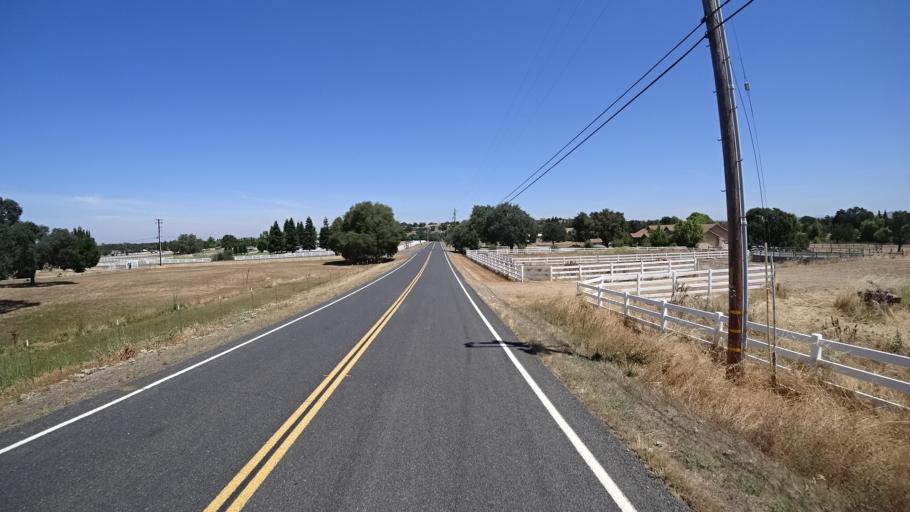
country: US
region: California
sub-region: Calaveras County
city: Rancho Calaveras
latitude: 38.1584
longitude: -120.9433
